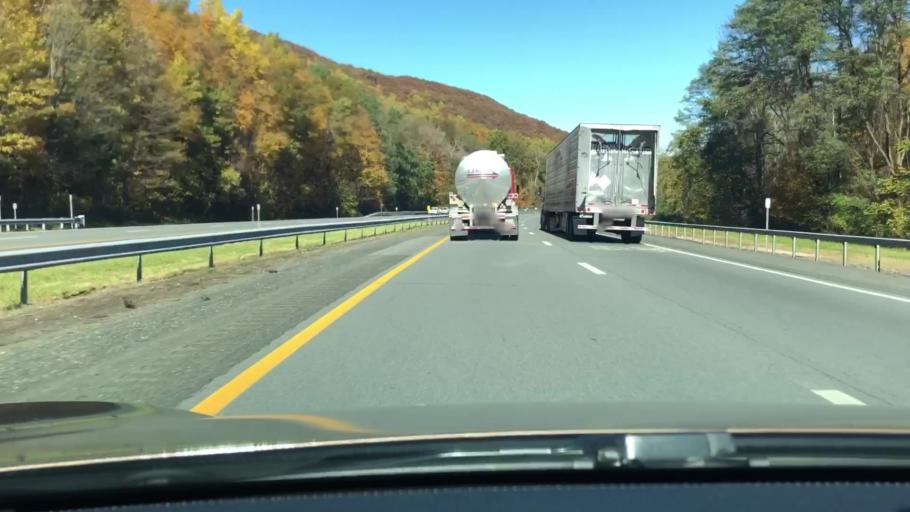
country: US
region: New York
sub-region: Orange County
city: Woodbury
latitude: 41.3791
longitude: -74.1032
